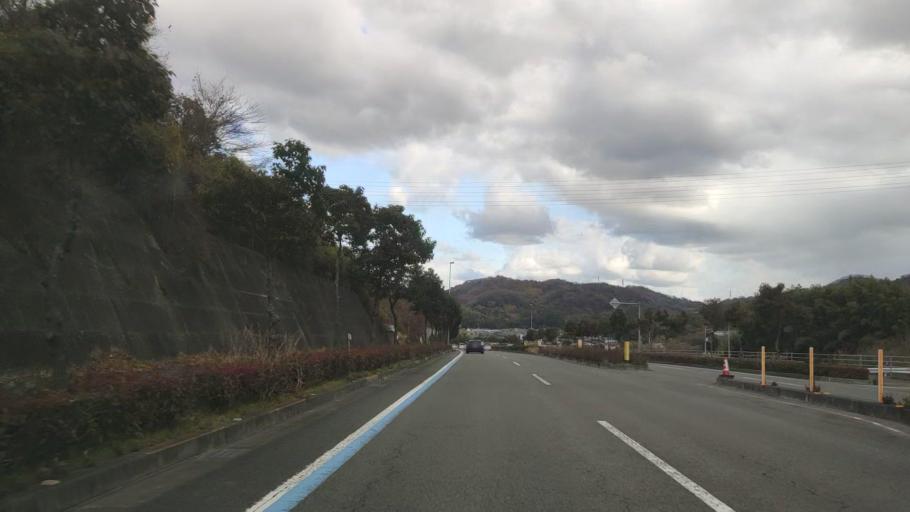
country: JP
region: Ehime
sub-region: Shikoku-chuo Shi
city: Matsuyama
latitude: 33.8917
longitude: 132.7574
